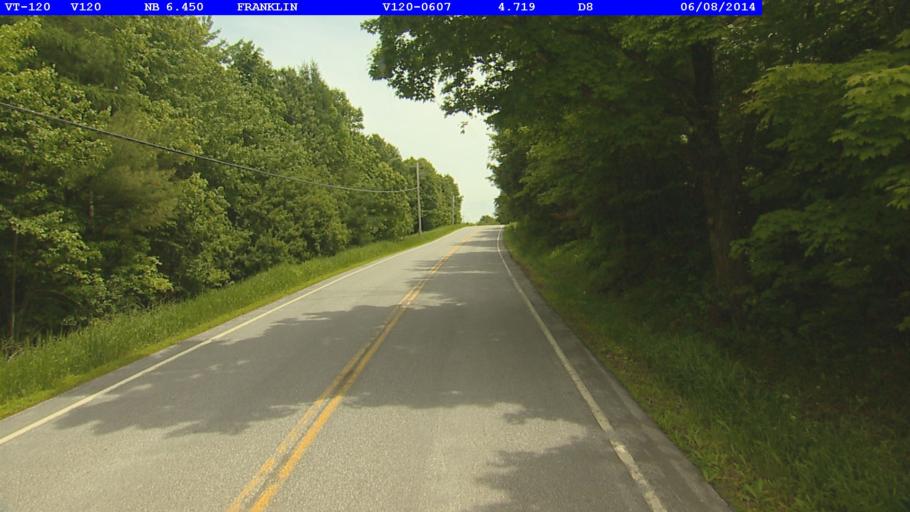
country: US
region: Vermont
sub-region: Franklin County
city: Enosburg Falls
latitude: 44.9863
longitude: -72.8990
